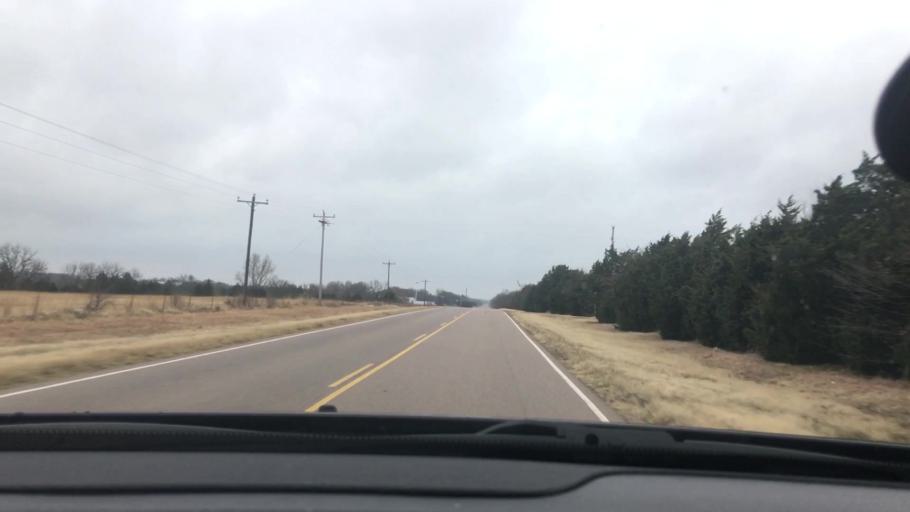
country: US
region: Oklahoma
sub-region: Johnston County
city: Tishomingo
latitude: 34.2805
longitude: -96.6711
